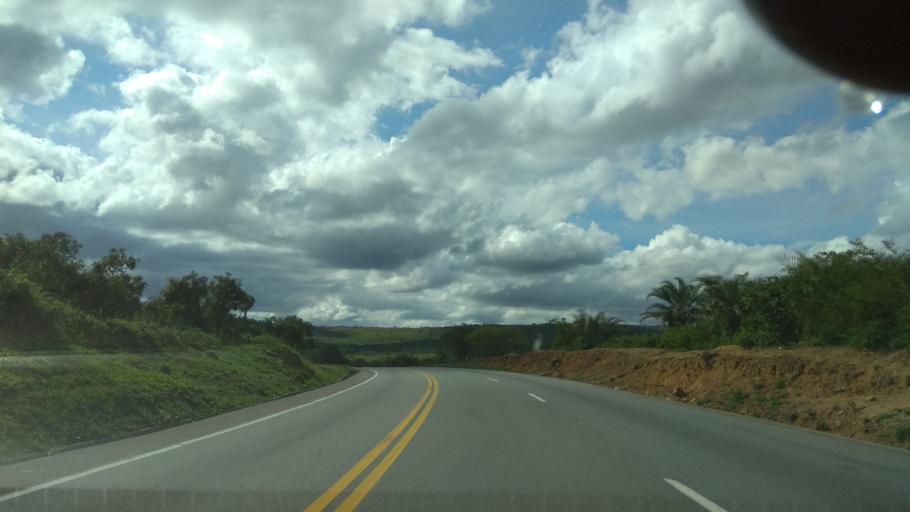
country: BR
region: Bahia
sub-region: Santa Ines
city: Santa Ines
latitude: -13.1278
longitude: -39.9906
